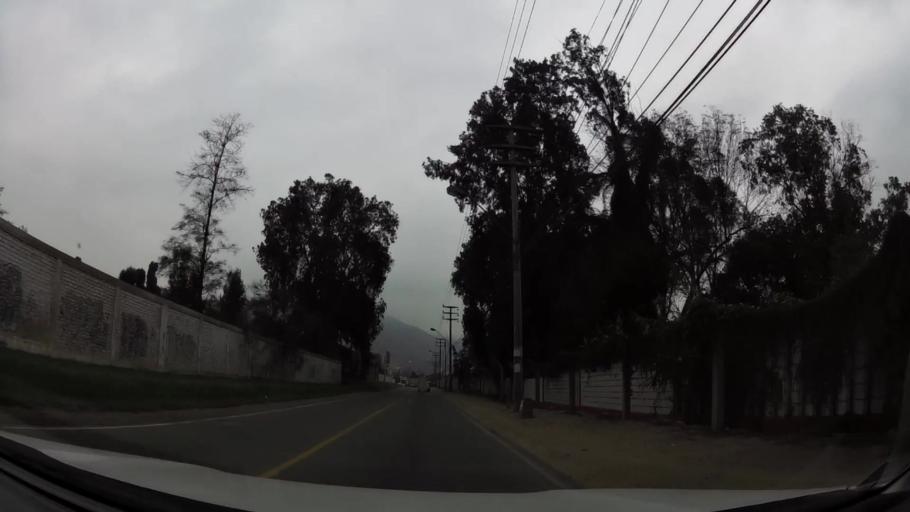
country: PE
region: Lima
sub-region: Lima
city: La Molina
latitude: -12.0799
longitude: -76.9294
